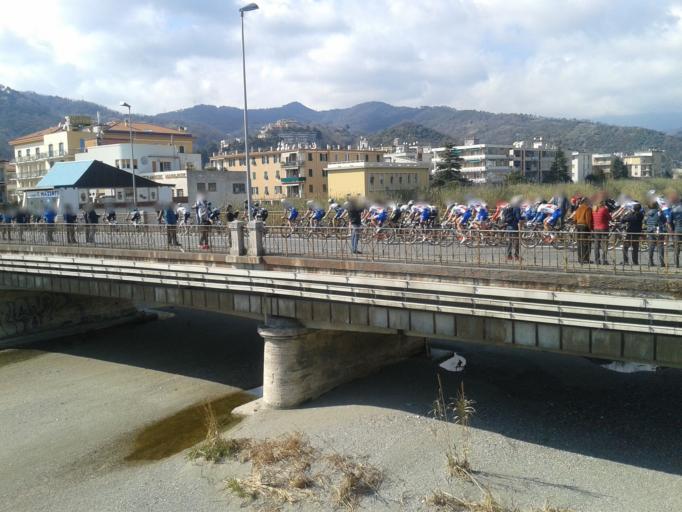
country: IT
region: Liguria
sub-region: Provincia di Savona
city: Albisola Marina
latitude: 44.3290
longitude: 8.5090
